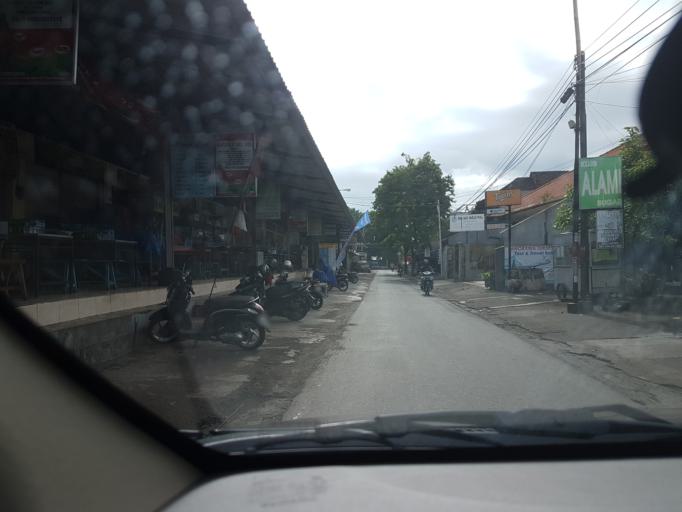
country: ID
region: Bali
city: Denpasar
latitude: -8.6621
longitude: 115.2074
